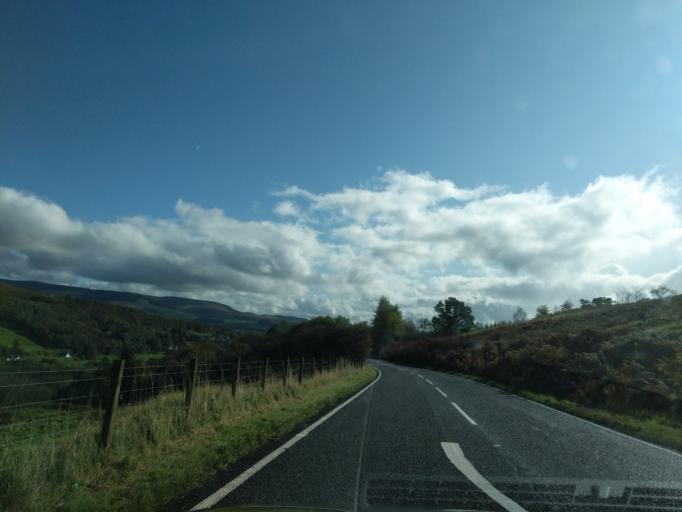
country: GB
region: Scotland
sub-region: Dumfries and Galloway
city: Moffat
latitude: 55.3514
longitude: -3.4649
